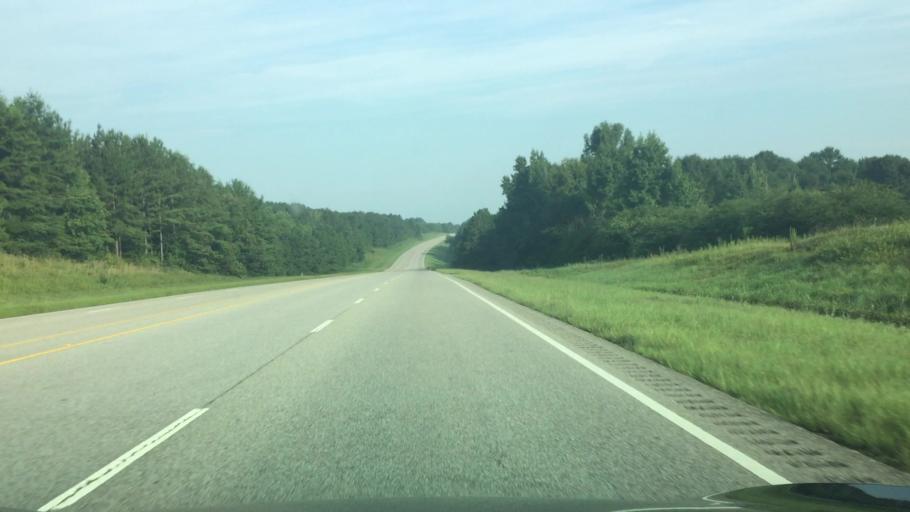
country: US
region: Alabama
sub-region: Covington County
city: Andalusia
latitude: 31.4474
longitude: -86.6205
